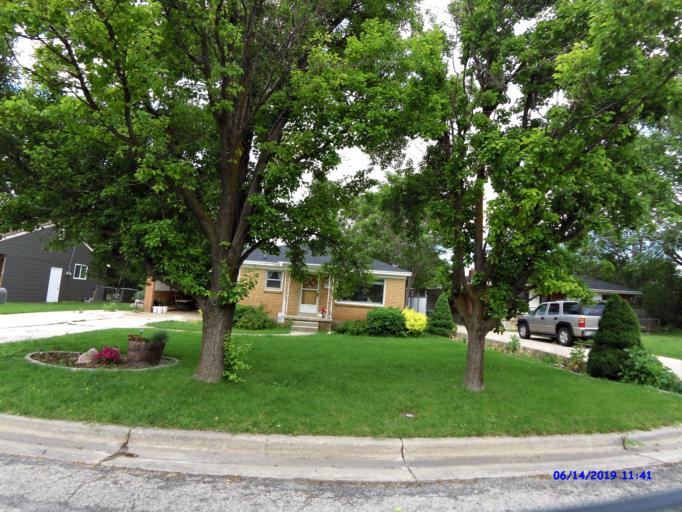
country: US
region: Utah
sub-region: Weber County
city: Ogden
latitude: 41.2529
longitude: -111.9469
